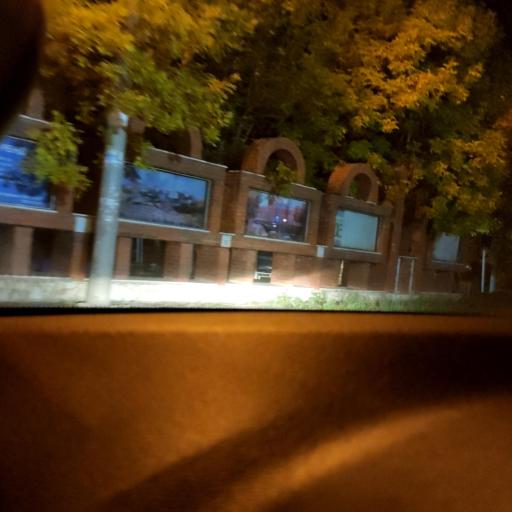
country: RU
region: Samara
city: Samara
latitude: 53.2169
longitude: 50.2418
